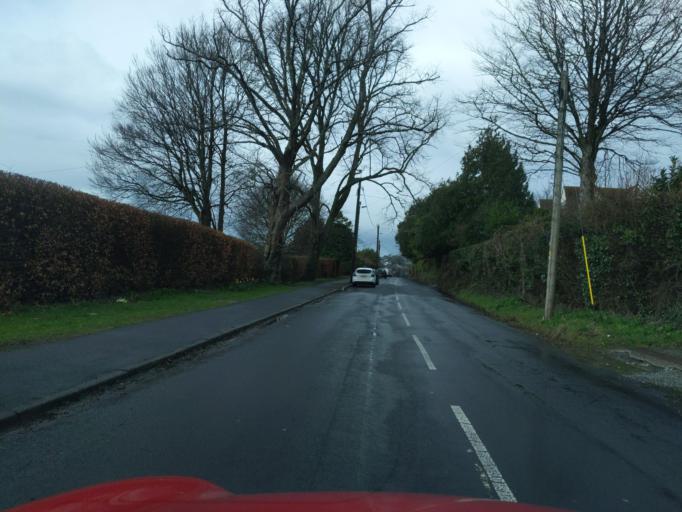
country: GB
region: England
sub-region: Devon
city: Tavistock
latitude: 50.5416
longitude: -4.1427
